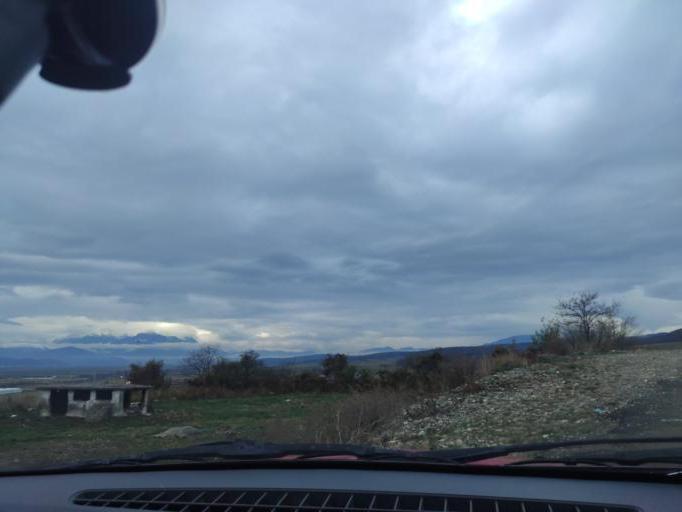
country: RO
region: Brasov
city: Codlea
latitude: 45.6938
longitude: 25.4366
